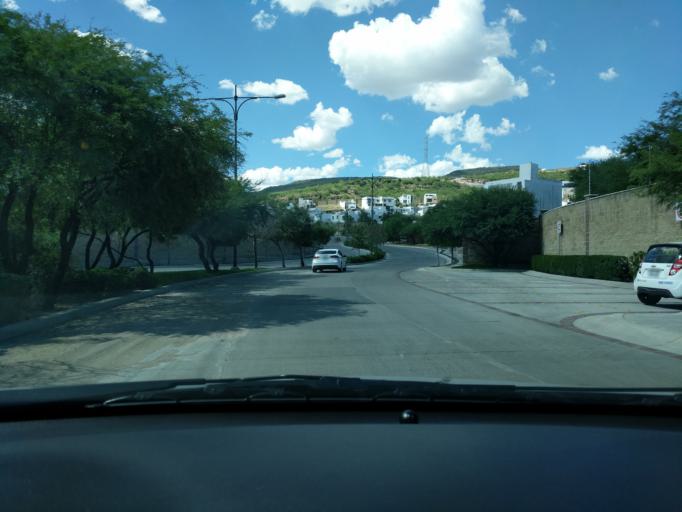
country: MX
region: Guanajuato
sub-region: Leon
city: Medina
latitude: 21.1333
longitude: -101.6043
